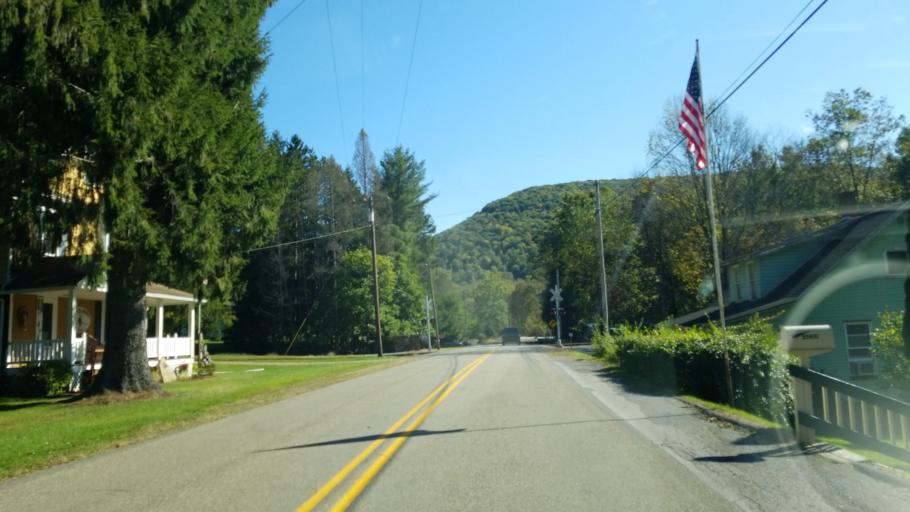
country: US
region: Pennsylvania
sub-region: Elk County
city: Saint Marys
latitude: 41.2870
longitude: -78.3947
